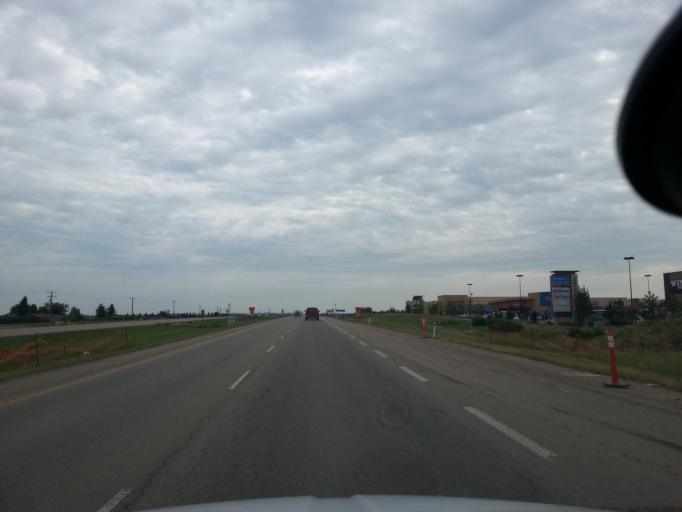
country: CA
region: Alberta
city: Sherwood Park
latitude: 53.5700
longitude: -113.2836
